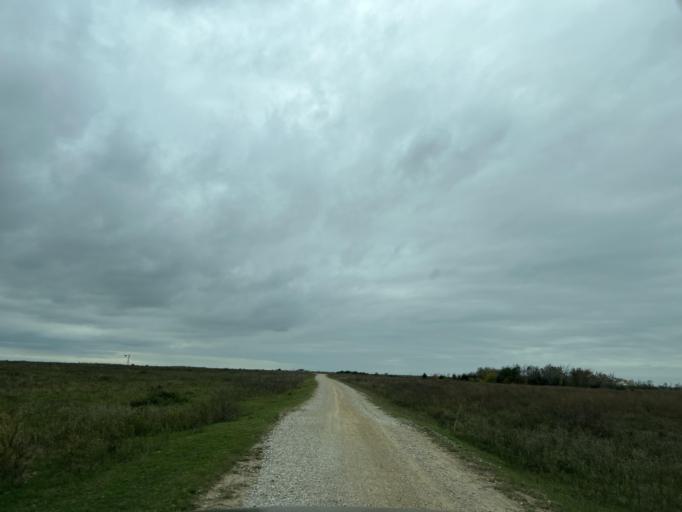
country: US
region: Texas
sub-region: Colorado County
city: Eagle Lake
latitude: 29.6740
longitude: -96.2882
